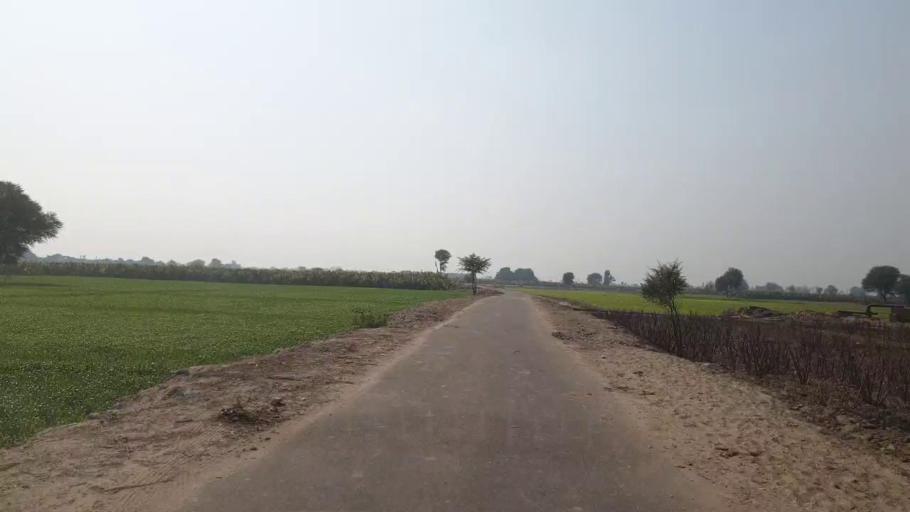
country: PK
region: Sindh
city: Bhit Shah
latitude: 25.7864
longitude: 68.4908
